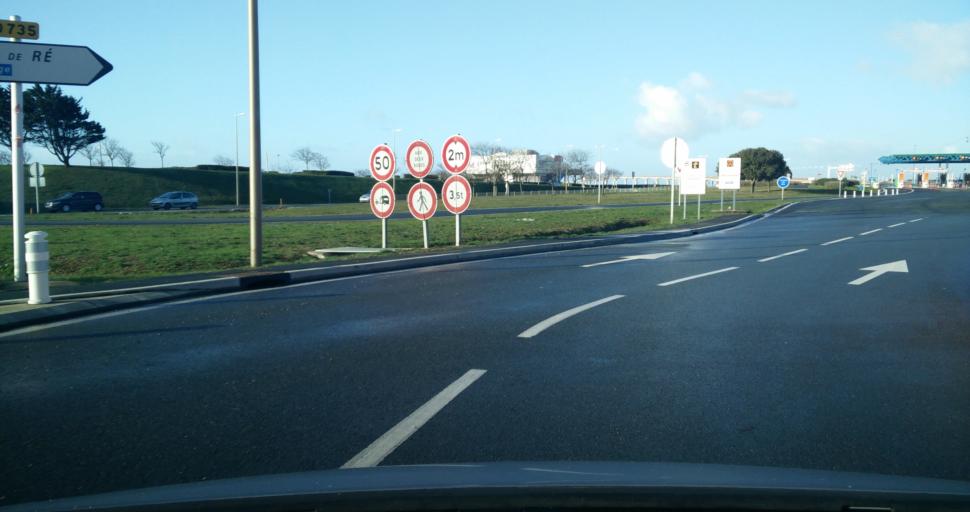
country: FR
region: Poitou-Charentes
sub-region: Departement de la Charente-Maritime
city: Rivedoux-Plage
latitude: 46.1756
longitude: -1.2162
